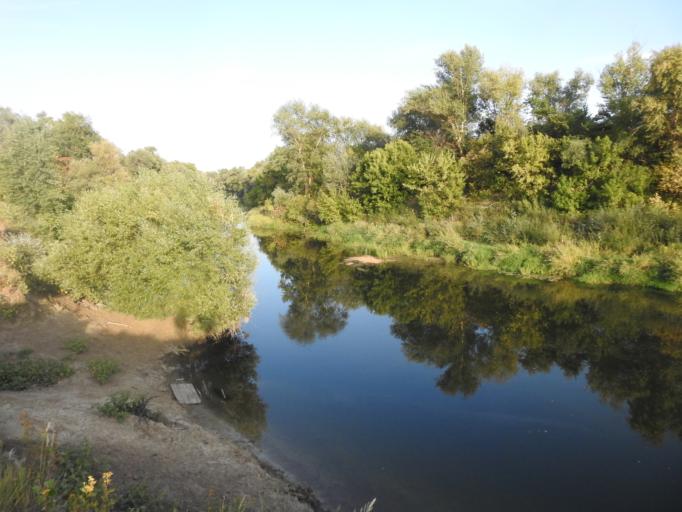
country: RU
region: Volgograd
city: Zhirnovsk
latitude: 51.1779
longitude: 44.9539
